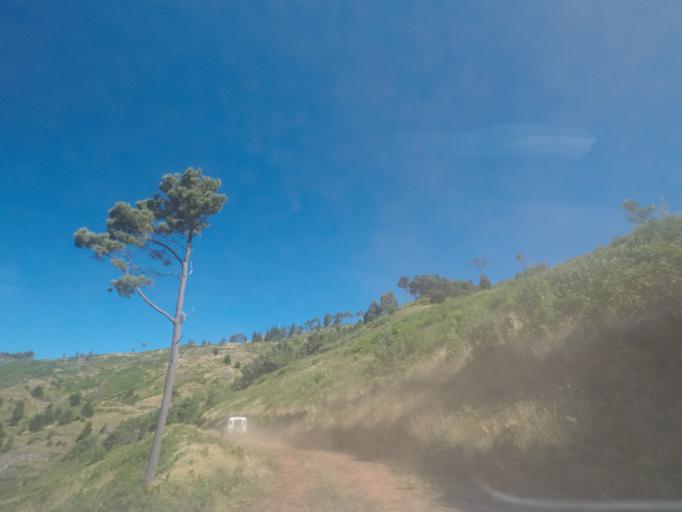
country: PT
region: Madeira
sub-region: Funchal
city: Nossa Senhora do Monte
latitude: 32.7036
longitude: -16.9072
